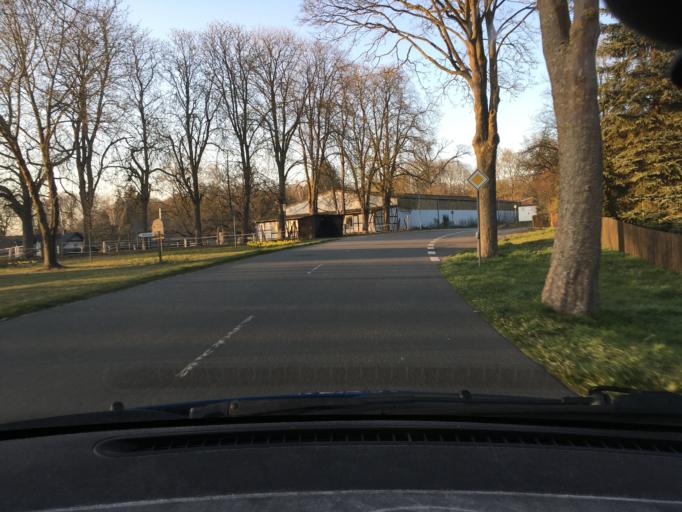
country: DE
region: Lower Saxony
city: Altenmedingen
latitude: 53.1684
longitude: 10.6175
